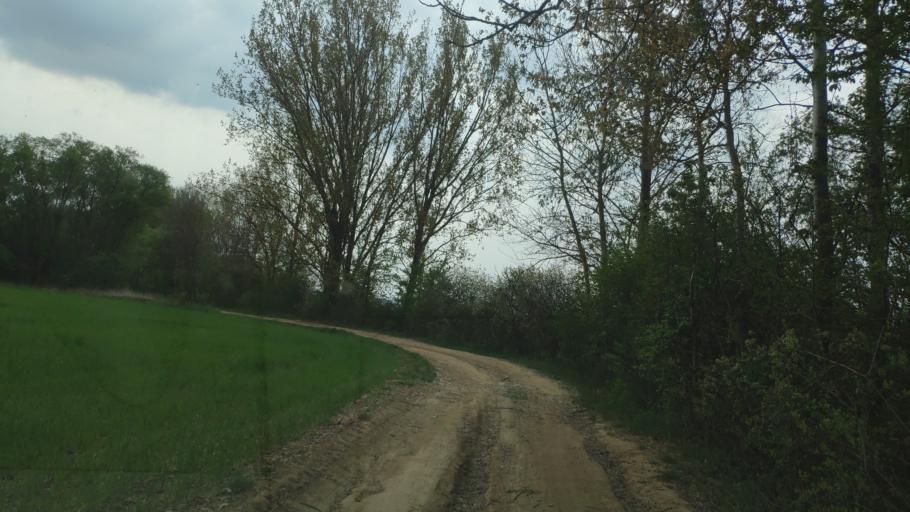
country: SK
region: Kosicky
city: Moldava nad Bodvou
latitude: 48.6128
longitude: 21.0388
